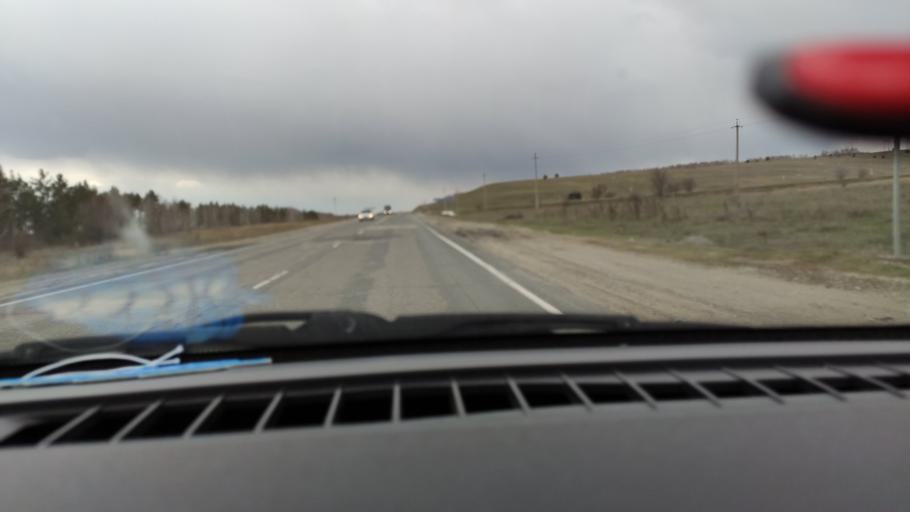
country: RU
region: Saratov
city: Sinodskoye
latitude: 52.0743
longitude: 46.7840
